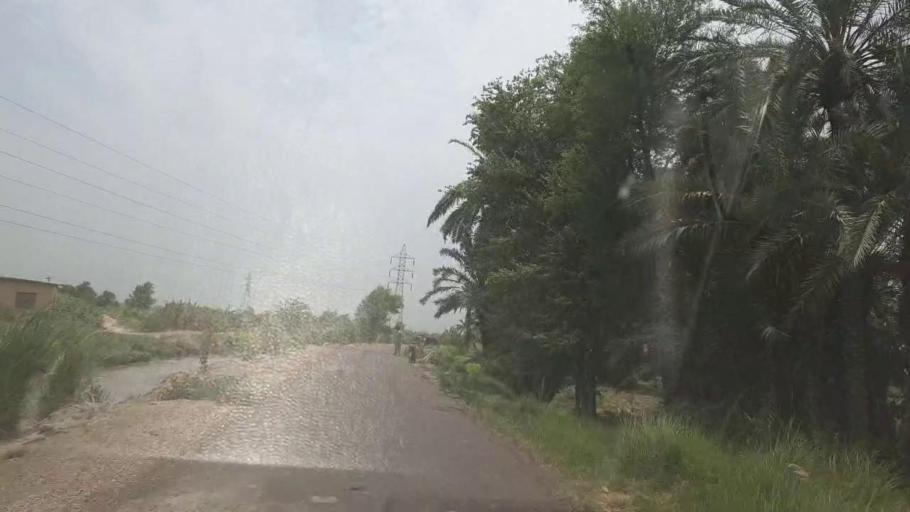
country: PK
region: Sindh
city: Kot Diji
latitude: 27.4213
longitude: 68.6466
